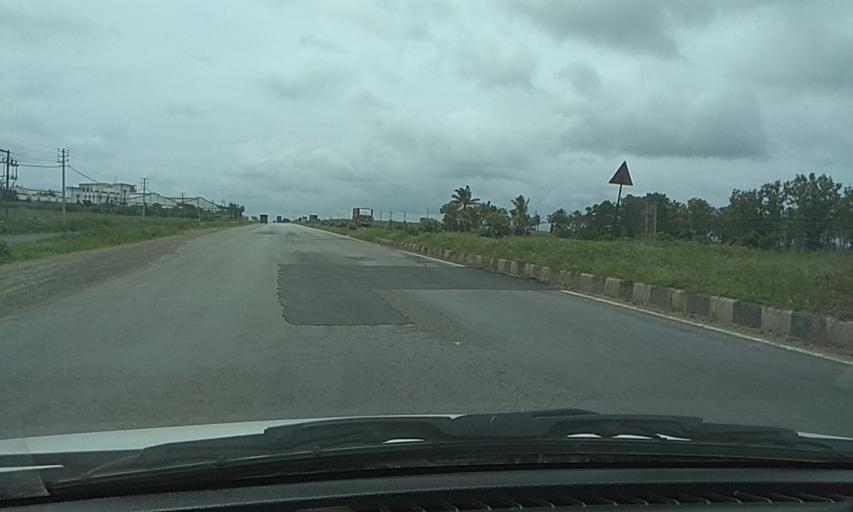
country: IN
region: Karnataka
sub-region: Davanagere
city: Mayakonda
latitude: 14.3387
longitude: 76.2106
